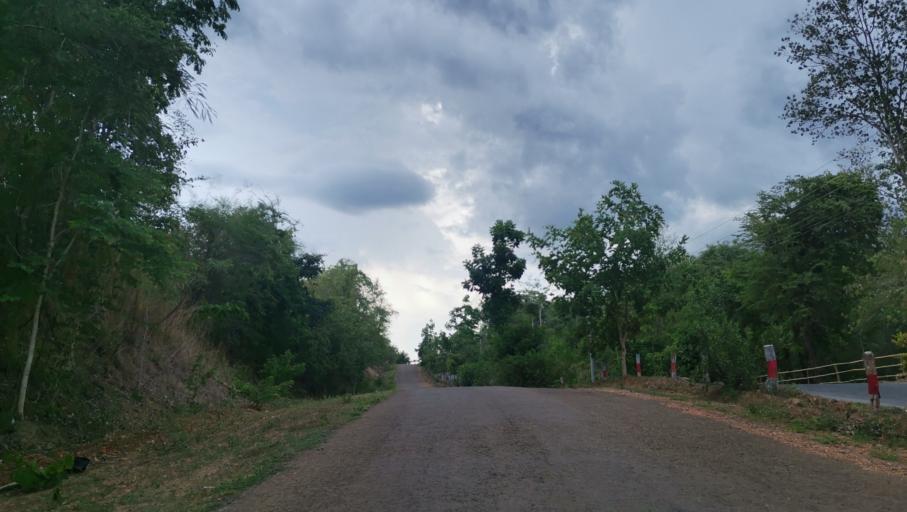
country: MM
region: Magway
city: Minbu
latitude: 20.0994
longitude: 94.5543
